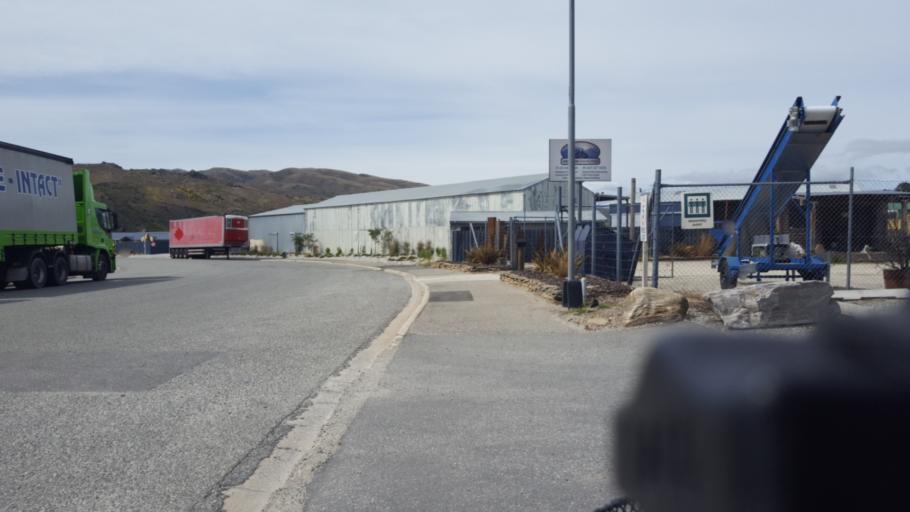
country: NZ
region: Otago
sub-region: Queenstown-Lakes District
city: Wanaka
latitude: -45.0523
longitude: 169.1939
